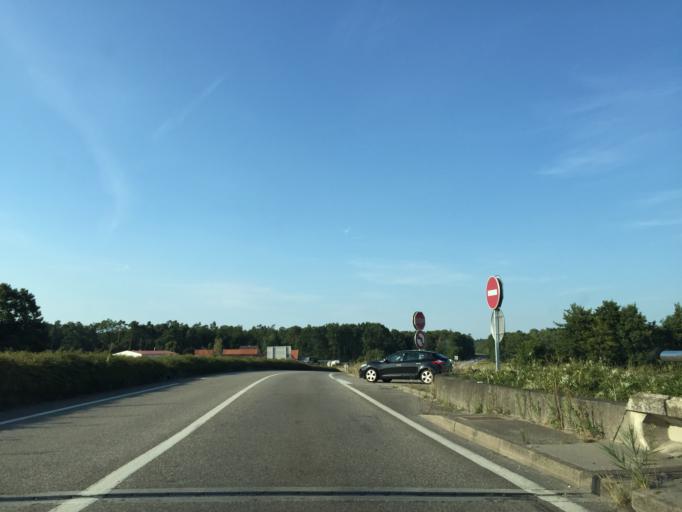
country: FR
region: Alsace
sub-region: Departement du Bas-Rhin
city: Haguenau
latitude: 48.8333
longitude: 7.7997
